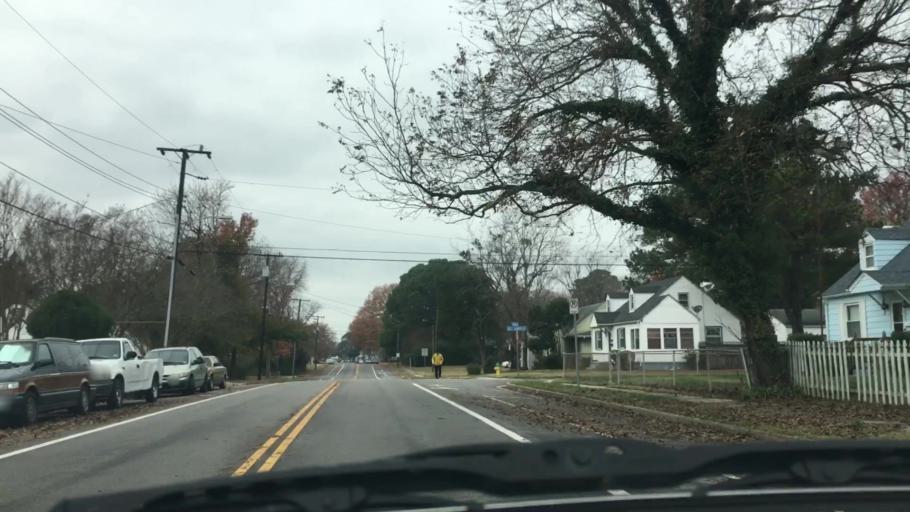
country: US
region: Virginia
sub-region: City of Norfolk
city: Norfolk
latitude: 36.8762
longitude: -76.2422
